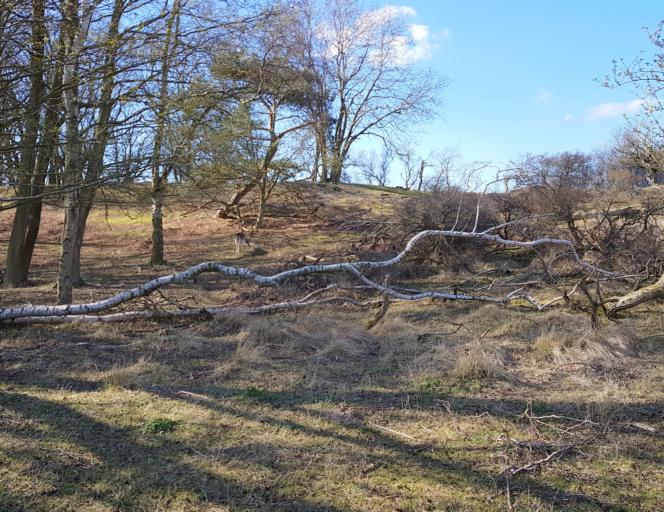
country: NL
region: South Holland
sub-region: Gemeente Hillegom
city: Hillegom
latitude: 52.3099
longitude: 4.5362
